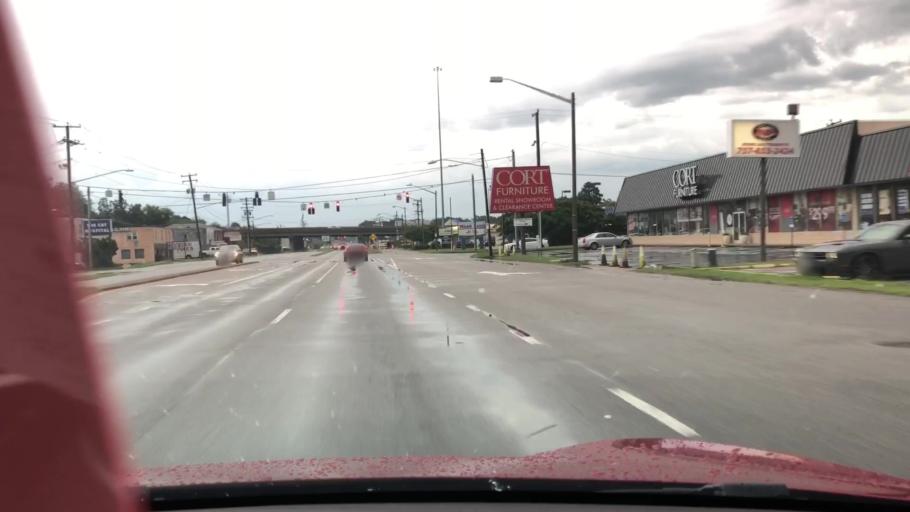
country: US
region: Virginia
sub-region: City of Chesapeake
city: Chesapeake
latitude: 36.8553
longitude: -76.1988
